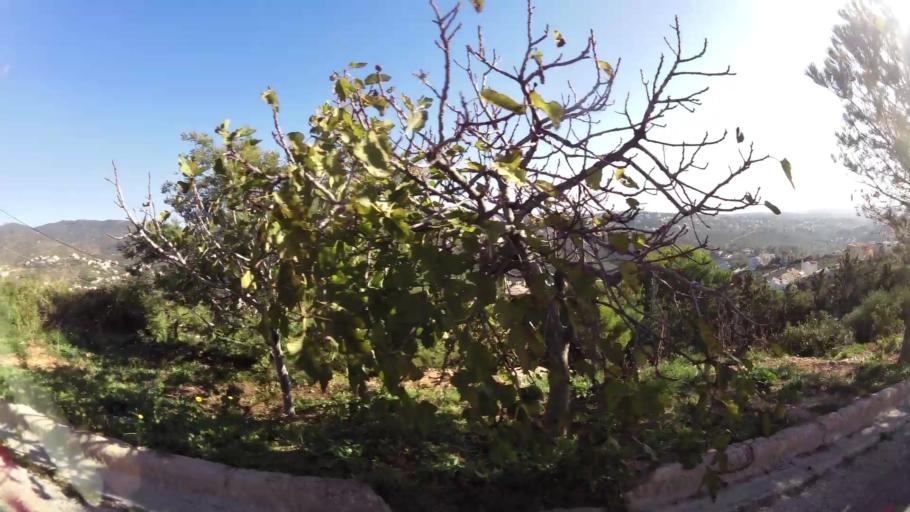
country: GR
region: Attica
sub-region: Nomarchia Anatolikis Attikis
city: Dhrafi
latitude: 38.0250
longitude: 23.9020
